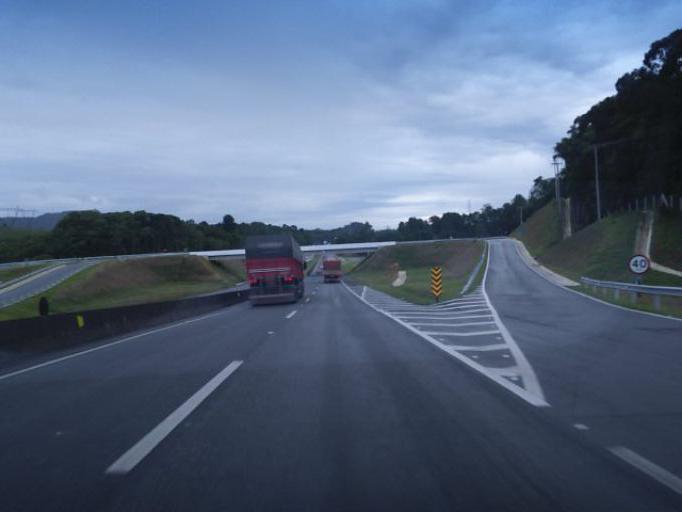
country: BR
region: Parana
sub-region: Sao Jose Dos Pinhais
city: Sao Jose dos Pinhais
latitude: -25.7270
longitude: -49.1348
